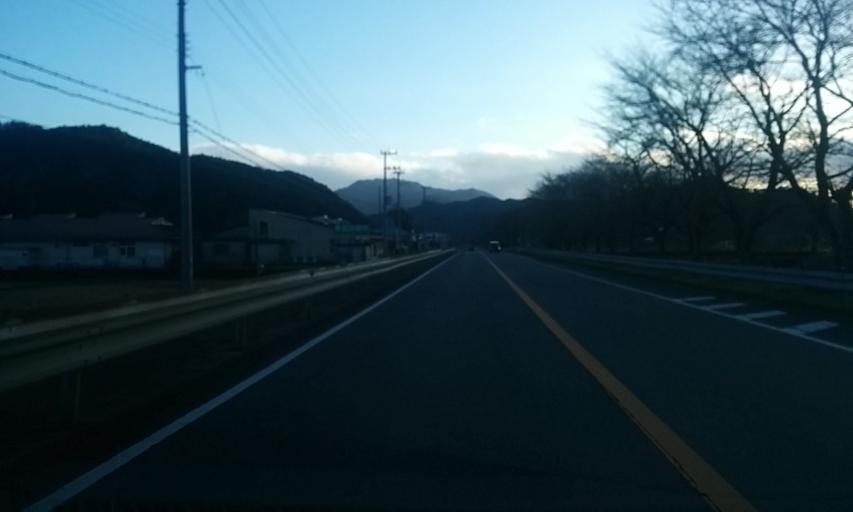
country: JP
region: Hyogo
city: Sasayama
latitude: 35.1037
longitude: 135.3176
